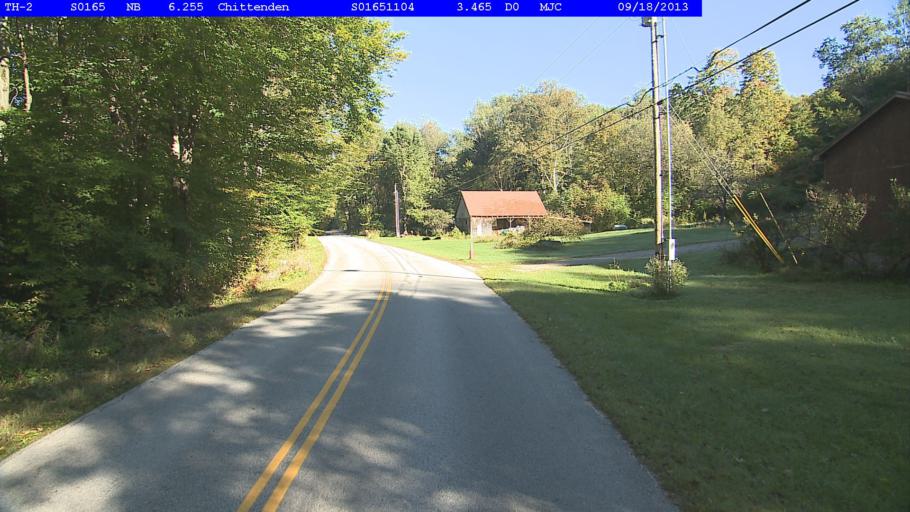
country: US
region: Vermont
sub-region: Rutland County
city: Rutland
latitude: 43.7243
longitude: -72.9681
